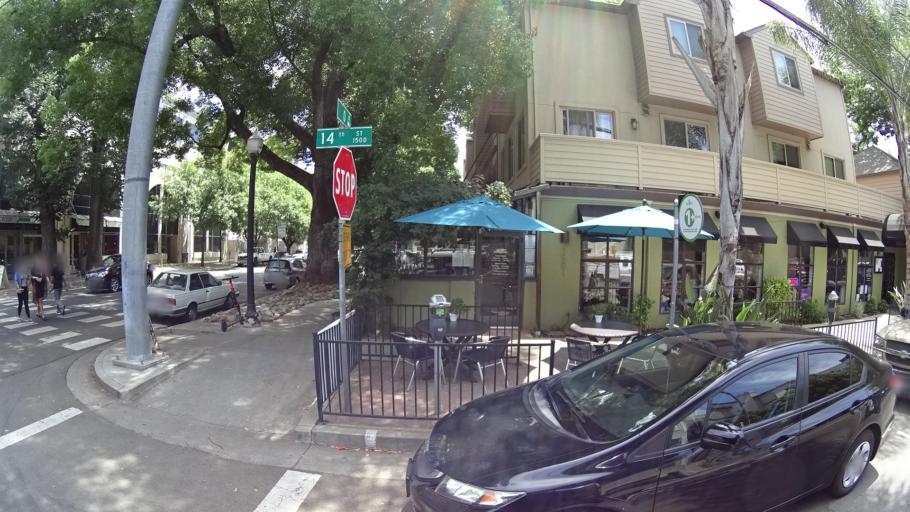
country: US
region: California
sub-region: Sacramento County
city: Sacramento
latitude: 38.5731
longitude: -121.4903
